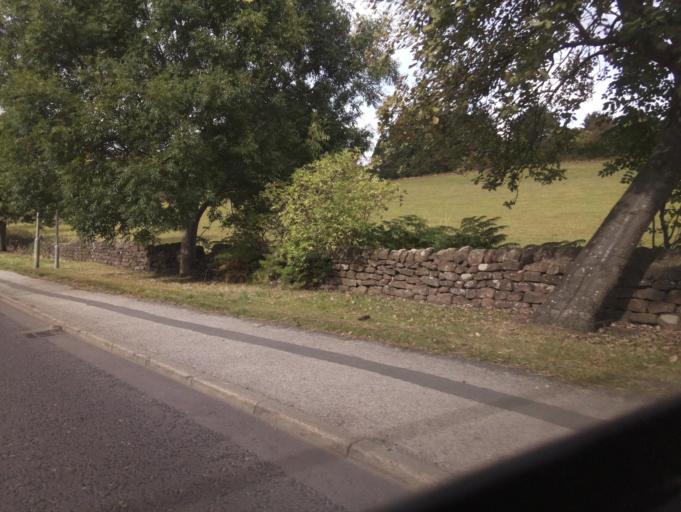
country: GB
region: England
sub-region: North Yorkshire
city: Harrogate
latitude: 54.0099
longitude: -1.5534
